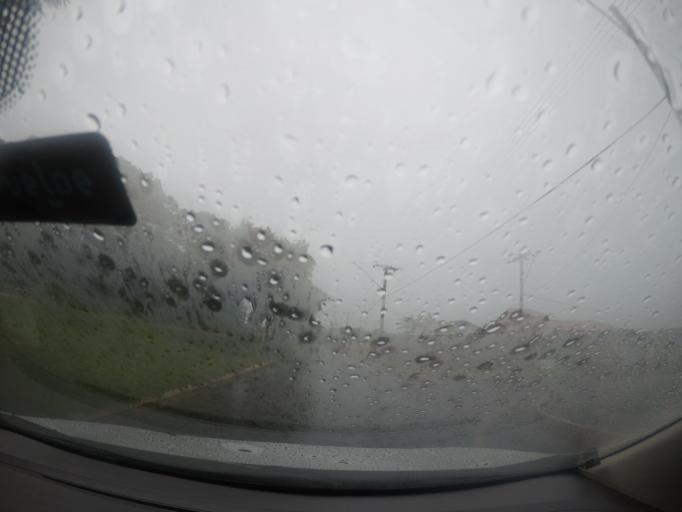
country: BR
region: Goias
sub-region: Goiania
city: Goiania
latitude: -16.5871
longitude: -49.3323
